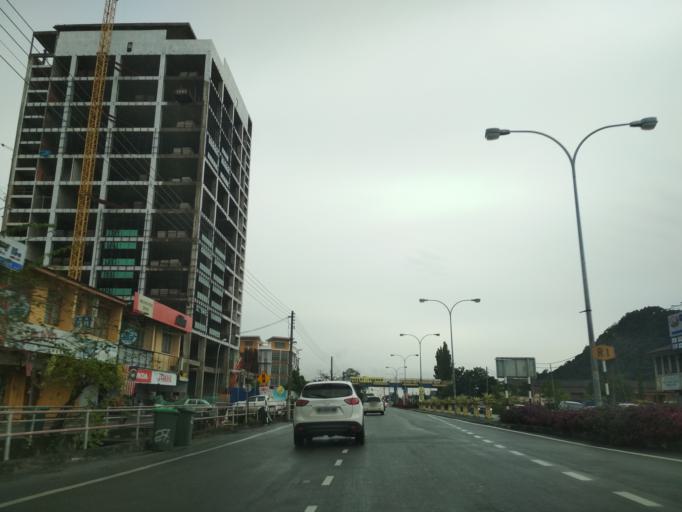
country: MY
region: Perlis
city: Kangar
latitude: 6.4353
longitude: 100.1950
